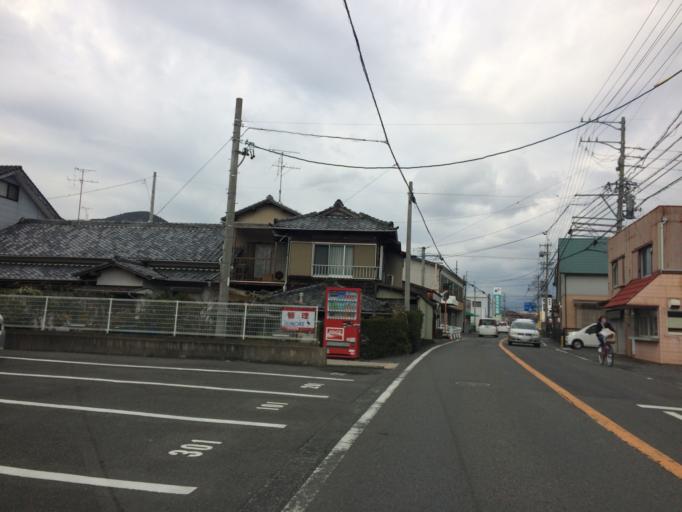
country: JP
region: Shizuoka
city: Shizuoka-shi
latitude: 34.9418
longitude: 138.3584
